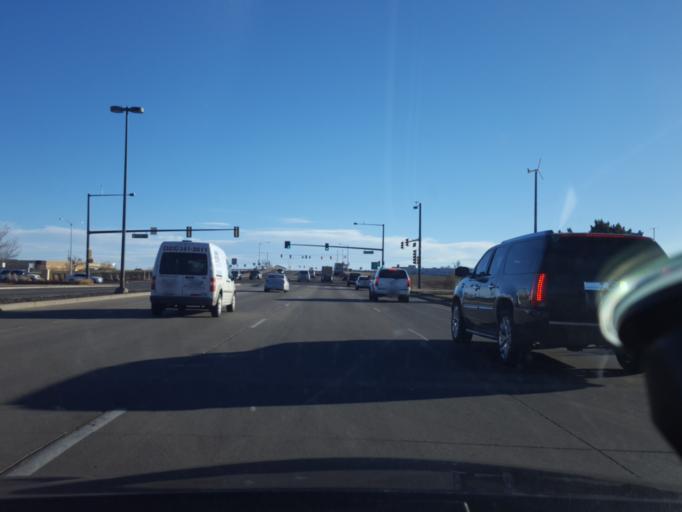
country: US
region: Colorado
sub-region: Adams County
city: Aurora
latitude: 39.7627
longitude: -104.7723
